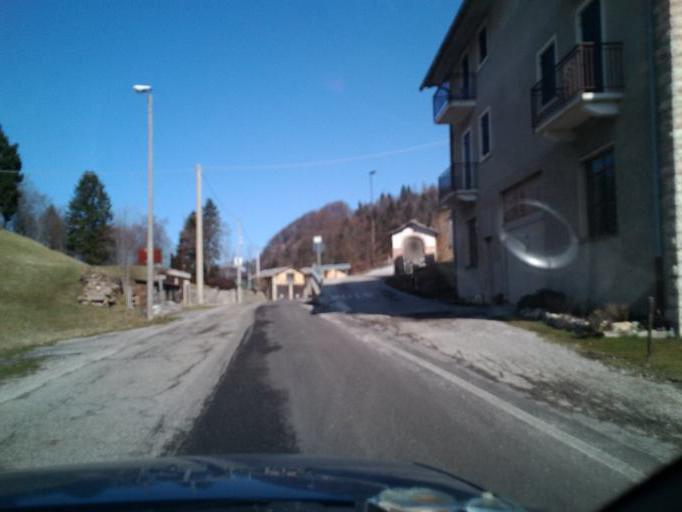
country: IT
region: Veneto
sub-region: Provincia di Verona
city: Bosco Chiesanuova
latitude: 45.6379
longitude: 11.0311
